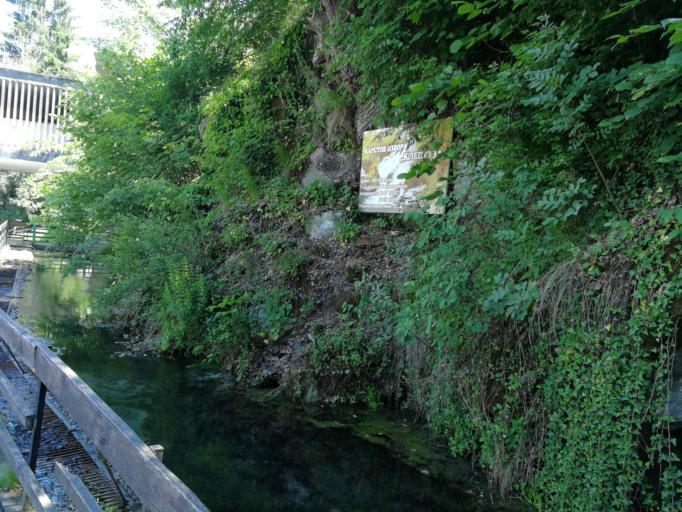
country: BG
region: Pazardzhik
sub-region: Obshtina Velingrad
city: Velingrad
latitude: 41.9990
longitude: 23.9819
